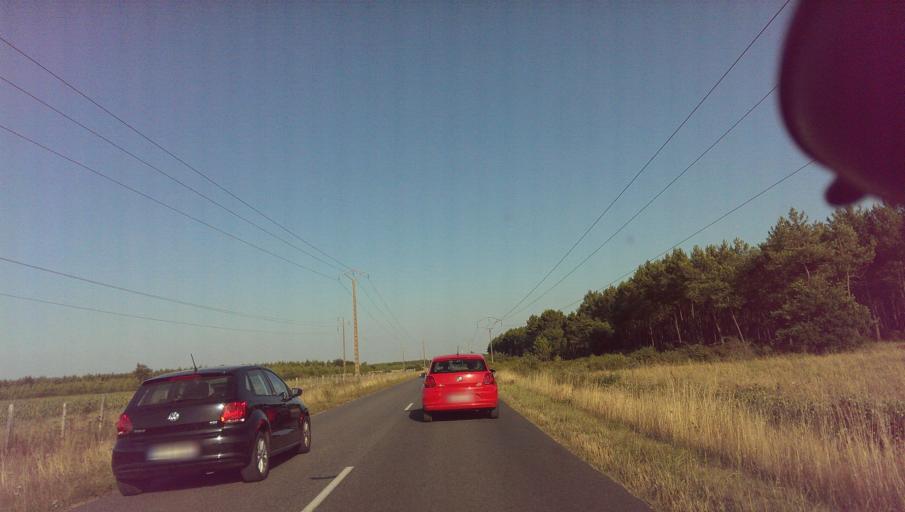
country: FR
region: Aquitaine
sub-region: Departement des Landes
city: Mimizan
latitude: 44.1857
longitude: -1.1977
